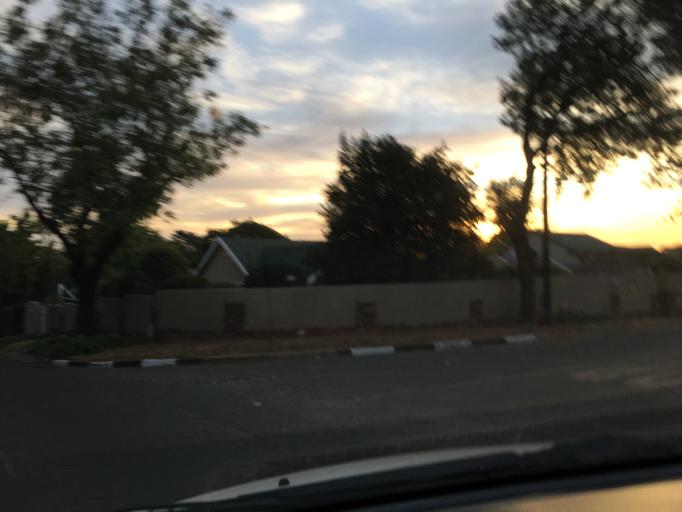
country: ZA
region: Gauteng
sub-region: City of Johannesburg Metropolitan Municipality
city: Johannesburg
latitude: -26.0810
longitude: 28.0052
